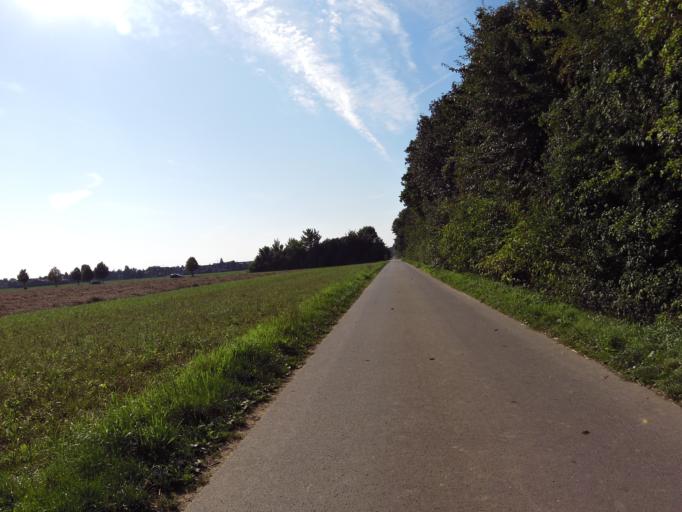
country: DE
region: North Rhine-Westphalia
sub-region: Regierungsbezirk Koln
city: Eschweiler
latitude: 50.8417
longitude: 6.2582
